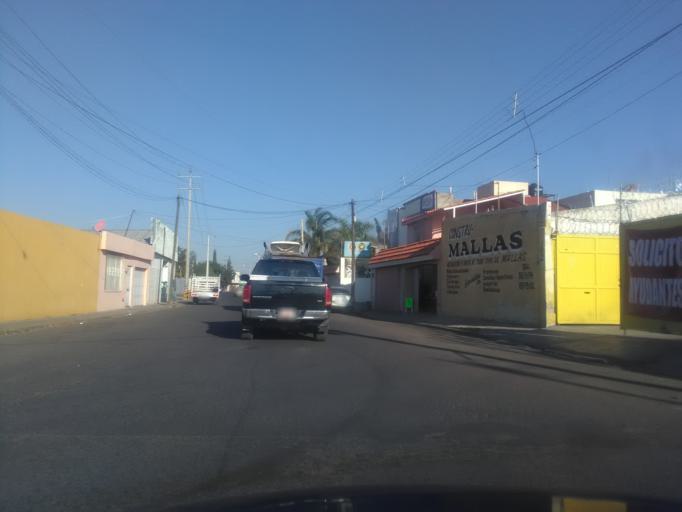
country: MX
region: Durango
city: Victoria de Durango
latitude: 24.0419
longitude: -104.6308
